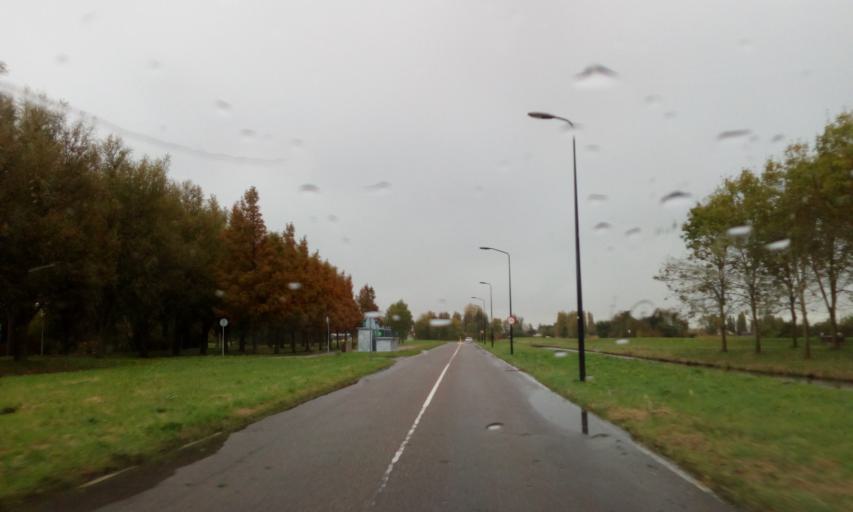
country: NL
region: South Holland
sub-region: Gemeente Rijswijk
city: Rijswijk
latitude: 52.0222
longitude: 4.3117
